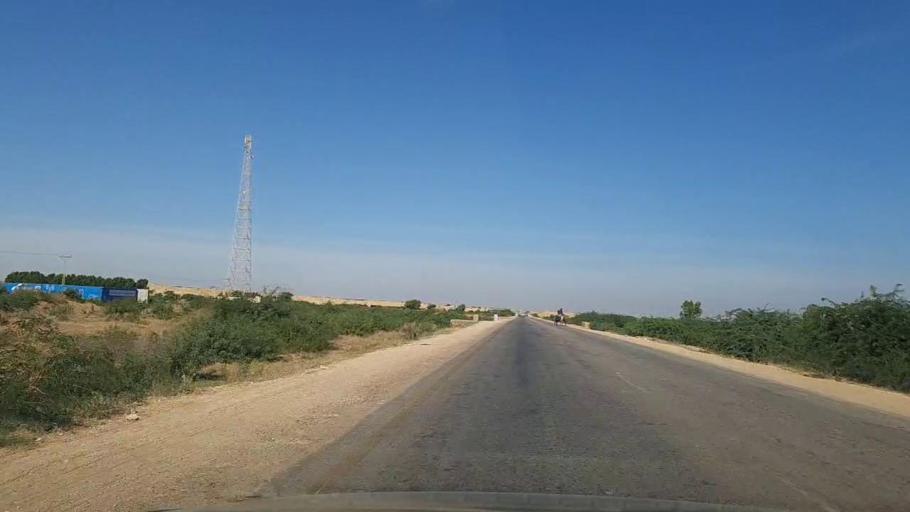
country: PK
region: Sindh
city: Kotri
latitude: 25.2045
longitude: 68.2374
